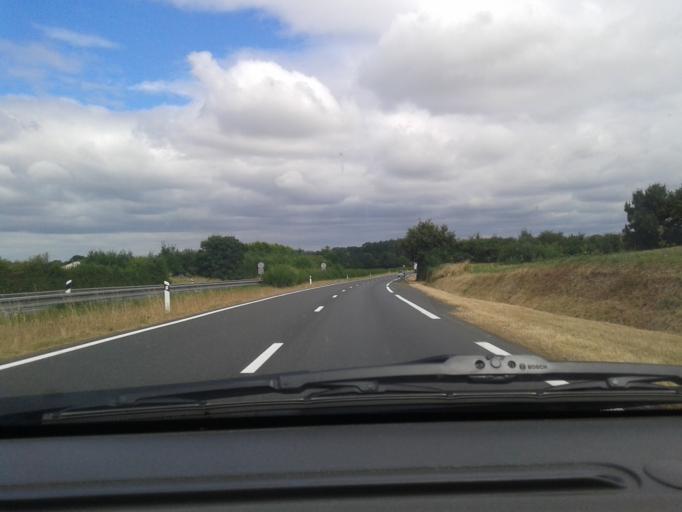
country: FR
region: Pays de la Loire
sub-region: Departement de Maine-et-Loire
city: Grez-Neuville
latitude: 47.6253
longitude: -0.7277
